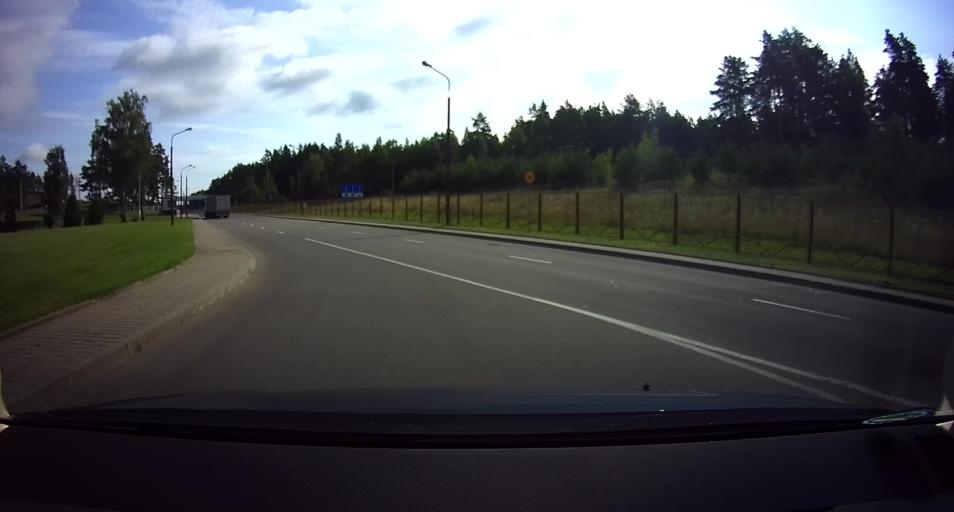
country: PL
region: Podlasie
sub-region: Powiat sokolski
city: Kuznica
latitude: 53.5234
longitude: 23.6683
